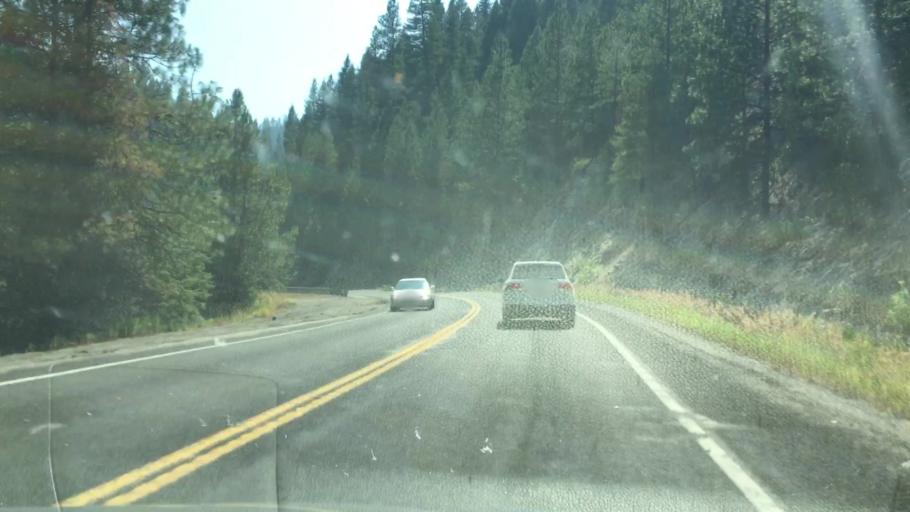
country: US
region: Idaho
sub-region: Valley County
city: Cascade
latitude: 44.2478
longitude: -116.0944
